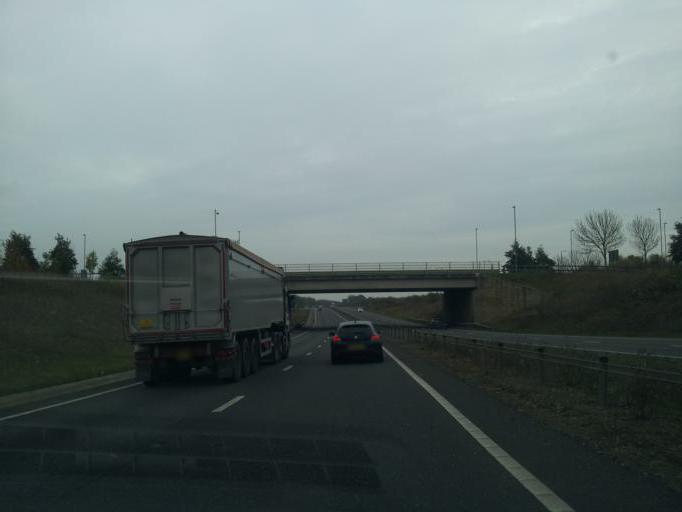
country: GB
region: England
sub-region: Cambridgeshire
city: Papworth Everard
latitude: 52.2250
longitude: -0.0735
